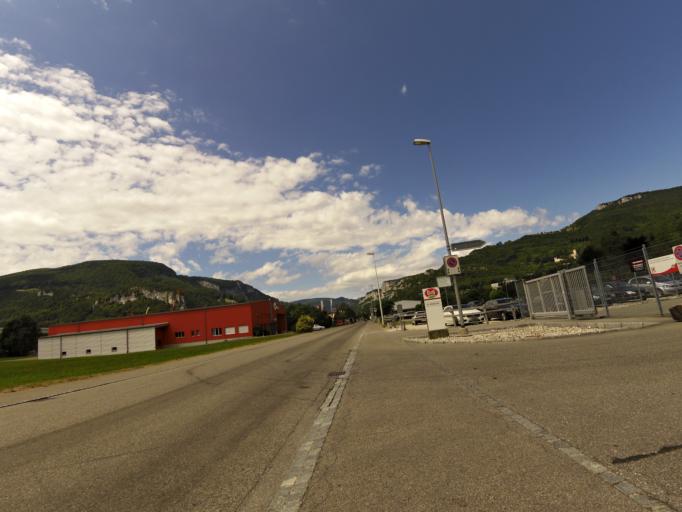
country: CH
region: Solothurn
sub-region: Bezirk Gaeu
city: Oensingen
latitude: 47.2828
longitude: 7.7180
